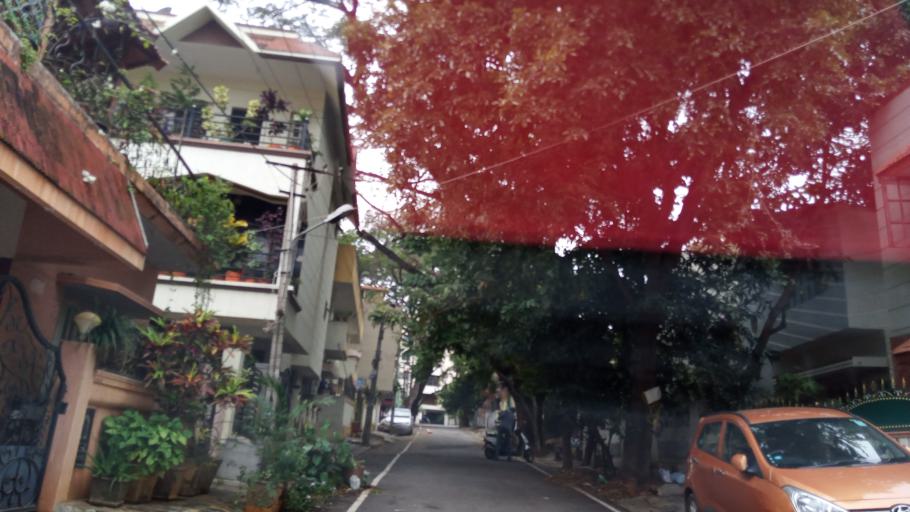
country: IN
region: Karnataka
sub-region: Bangalore Urban
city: Bangalore
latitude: 12.9389
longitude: 77.5401
